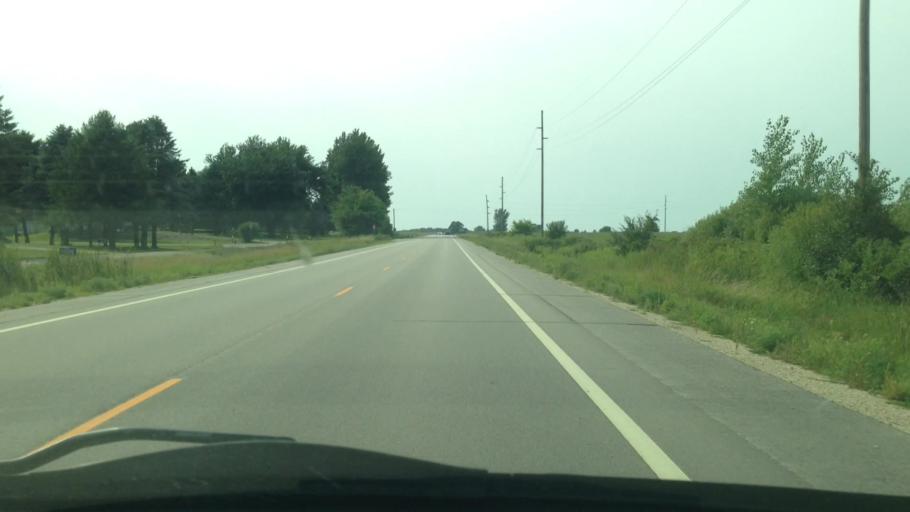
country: US
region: Minnesota
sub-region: Olmsted County
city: Eyota
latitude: 43.9947
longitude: -92.2358
